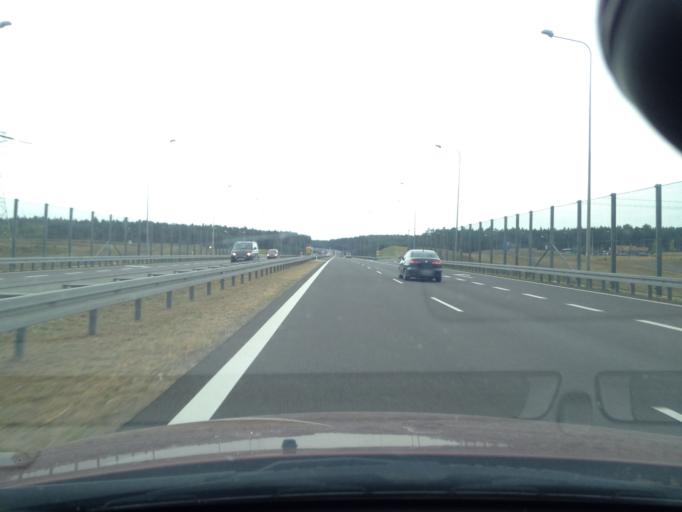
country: PL
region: Lubusz
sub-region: Powiat miedzyrzecki
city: Skwierzyna
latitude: 52.5384
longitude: 15.5418
